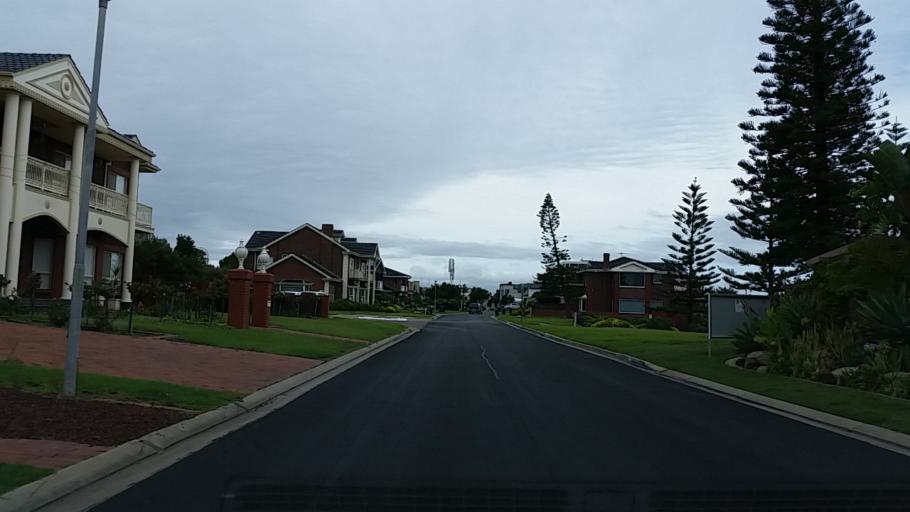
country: AU
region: South Australia
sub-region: Charles Sturt
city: West Lakes Shore
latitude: -34.8734
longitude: 138.4879
